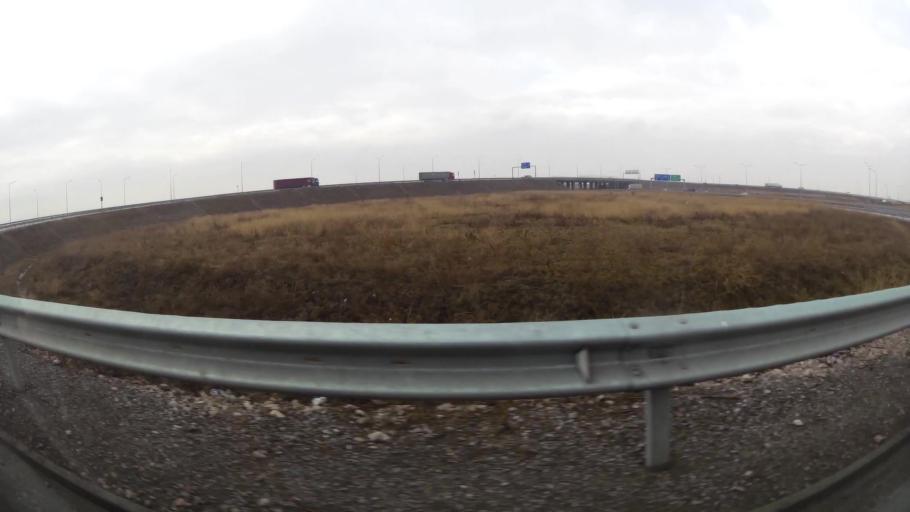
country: BG
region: Sofia-Capital
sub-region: Stolichna Obshtina
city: Sofia
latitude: 42.7693
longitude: 23.2903
